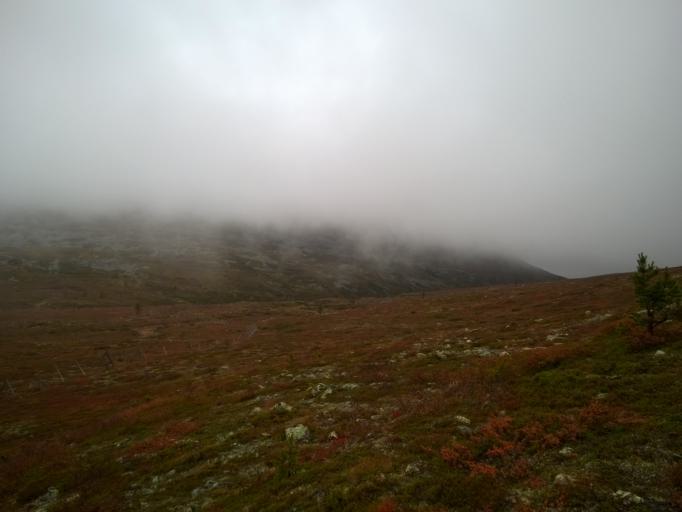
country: FI
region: Lapland
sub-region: Tunturi-Lappi
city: Muonio
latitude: 68.0553
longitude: 24.0825
